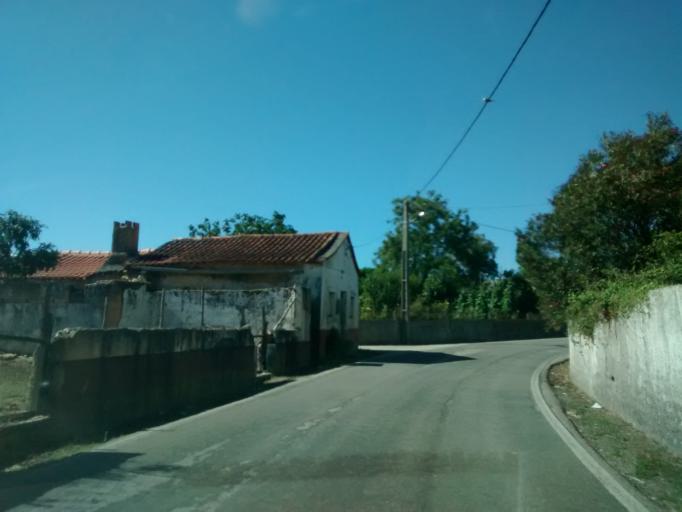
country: PT
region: Aveiro
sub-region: Anadia
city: Sangalhos
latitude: 40.4447
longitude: -8.5063
